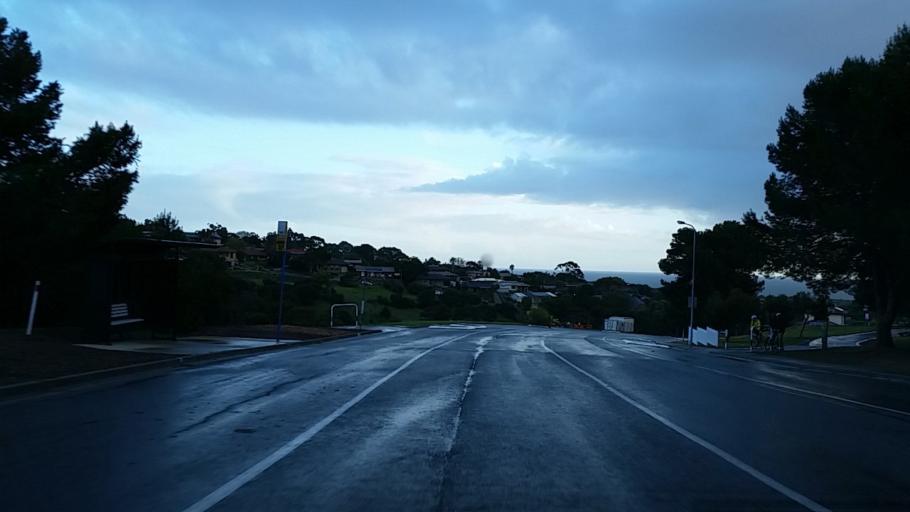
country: AU
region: South Australia
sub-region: Marion
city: Marino
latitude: -35.0703
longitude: 138.5102
